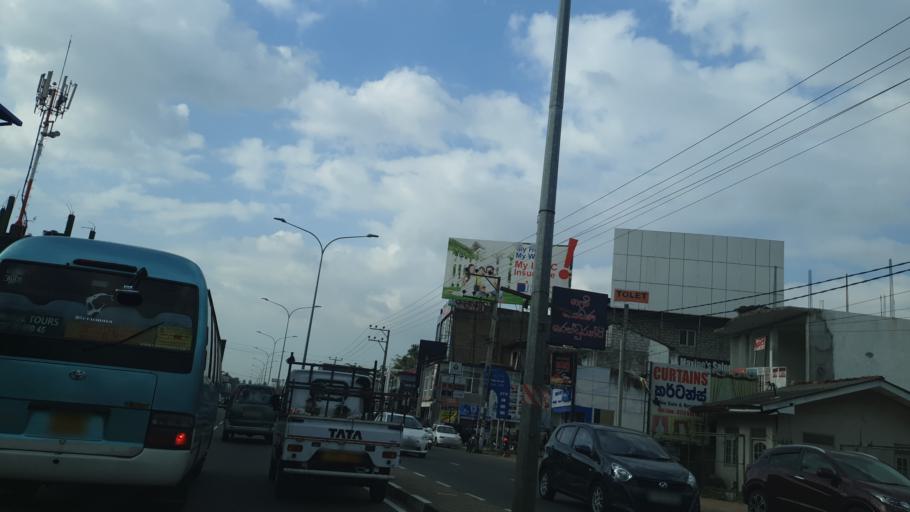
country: LK
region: Western
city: Maharagama
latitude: 6.8193
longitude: 79.9171
